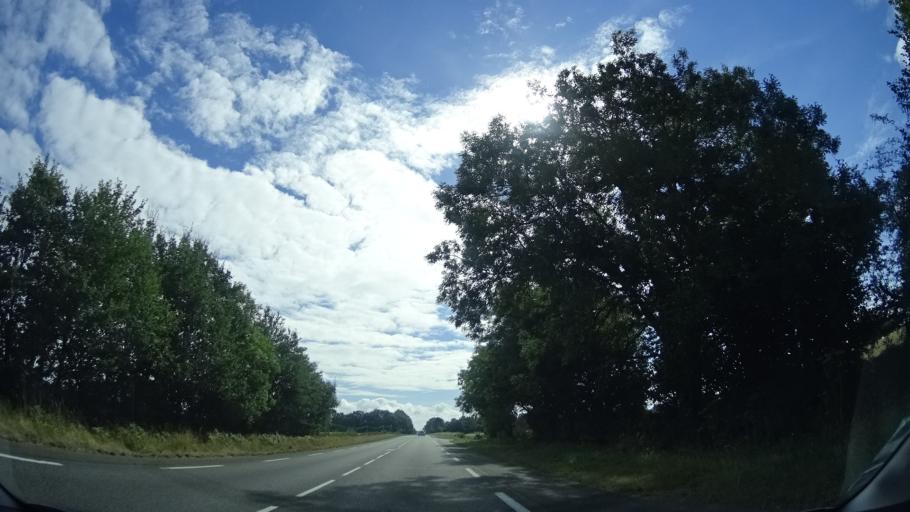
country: FR
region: Pays de la Loire
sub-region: Departement de la Mayenne
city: Loiron
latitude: 48.0715
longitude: -0.9495
